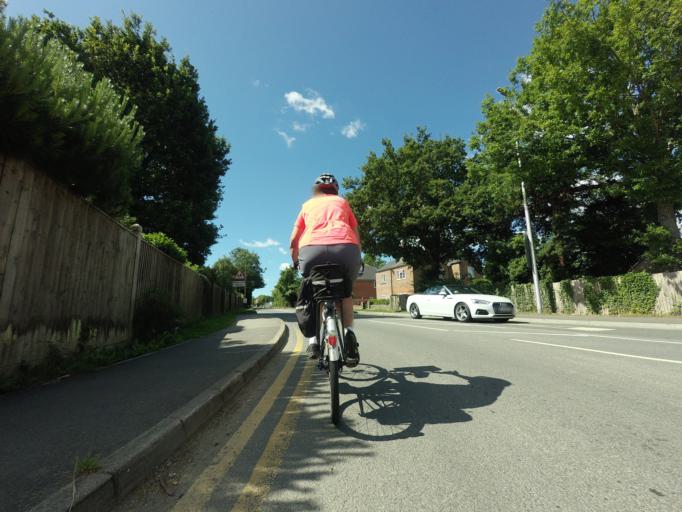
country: GB
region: England
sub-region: East Sussex
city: Horam
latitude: 50.9324
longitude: 0.2425
